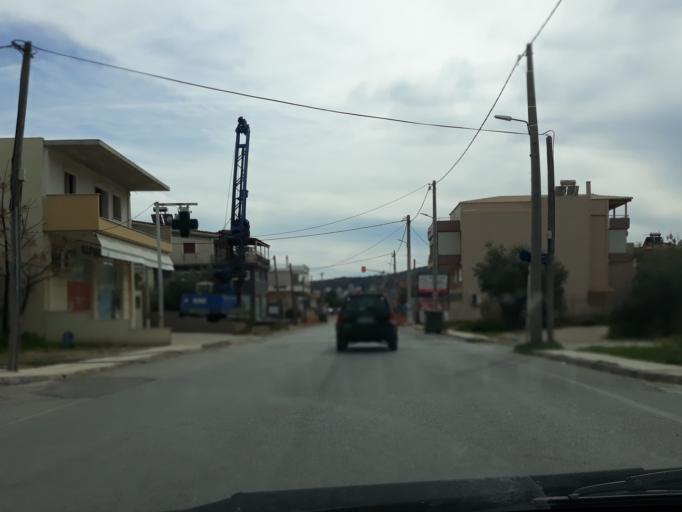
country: GR
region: Attica
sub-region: Nomarchia Dytikis Attikis
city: Ano Liosia
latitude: 38.0818
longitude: 23.7104
